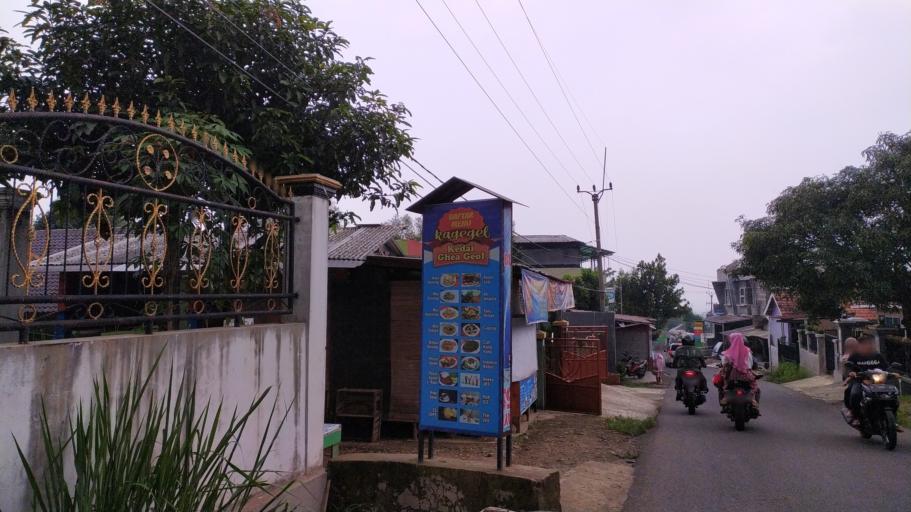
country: ID
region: West Java
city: Ciampea
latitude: -6.6076
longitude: 106.6993
